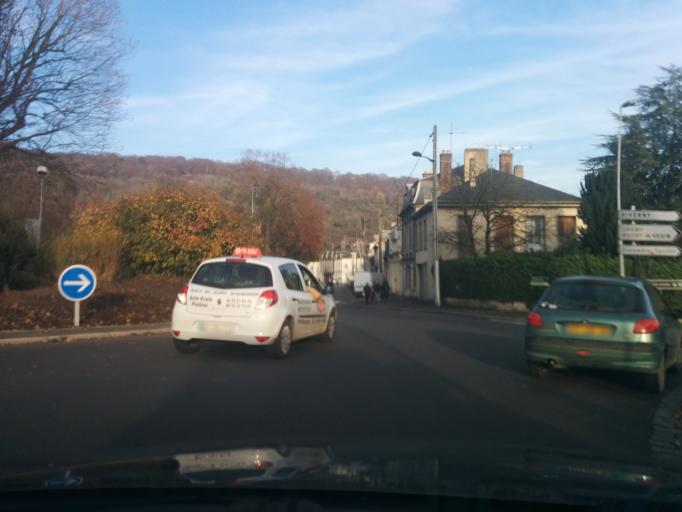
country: FR
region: Haute-Normandie
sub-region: Departement de l'Eure
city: Vernon
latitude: 49.0965
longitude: 1.4898
